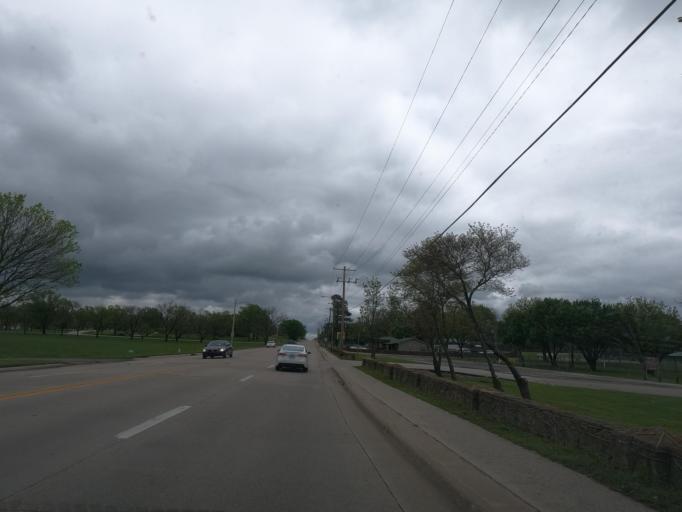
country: US
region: Kansas
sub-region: Labette County
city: Parsons
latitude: 37.3405
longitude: -95.2471
